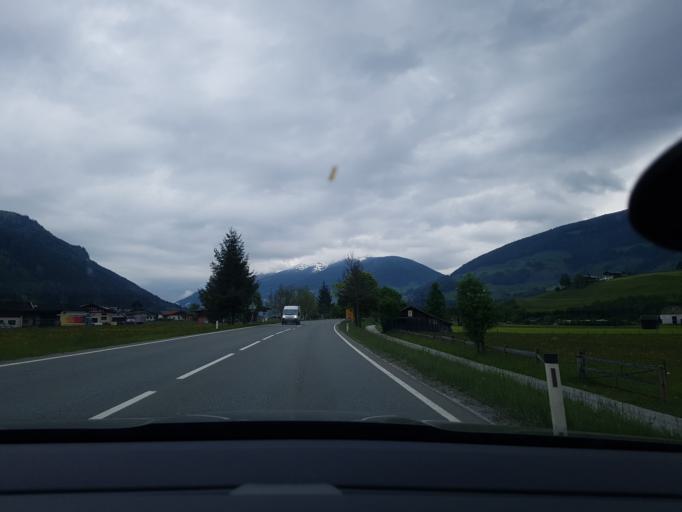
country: AT
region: Salzburg
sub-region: Politischer Bezirk Zell am See
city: Hollersbach im Pinzgau
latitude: 47.2758
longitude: 12.4293
